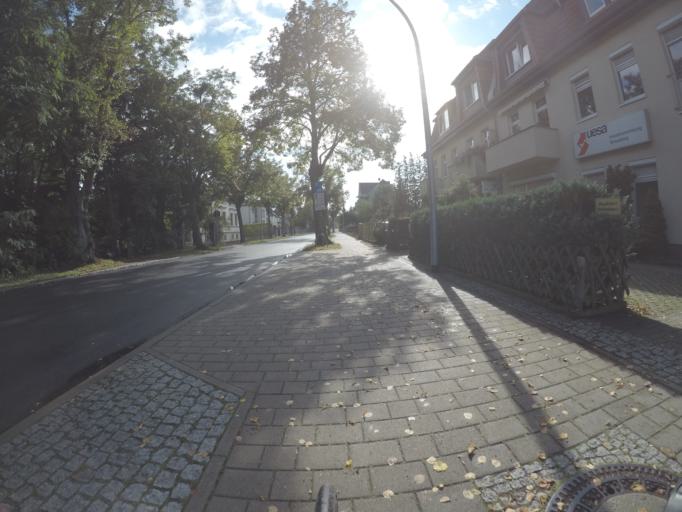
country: DE
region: Brandenburg
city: Rehfelde
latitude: 52.5342
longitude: 13.8459
